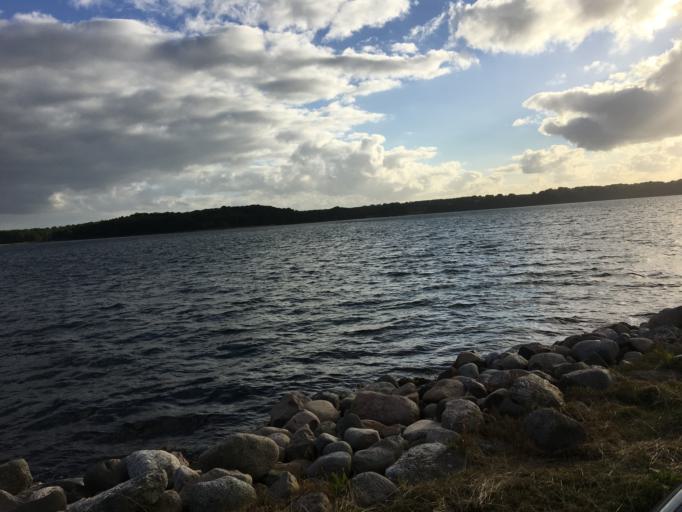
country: DK
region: South Denmark
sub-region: Middelfart Kommune
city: Middelfart
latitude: 55.4902
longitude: 9.7275
